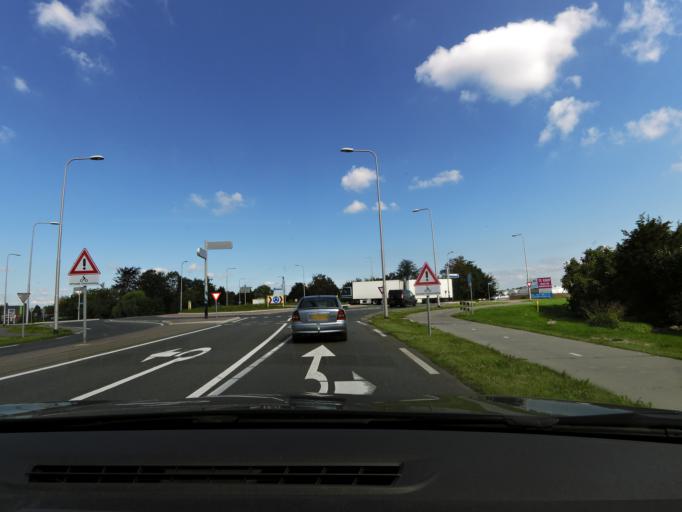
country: NL
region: North Holland
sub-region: Gemeente Uithoorn
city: Uithoorn
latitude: 52.2639
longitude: 4.7988
